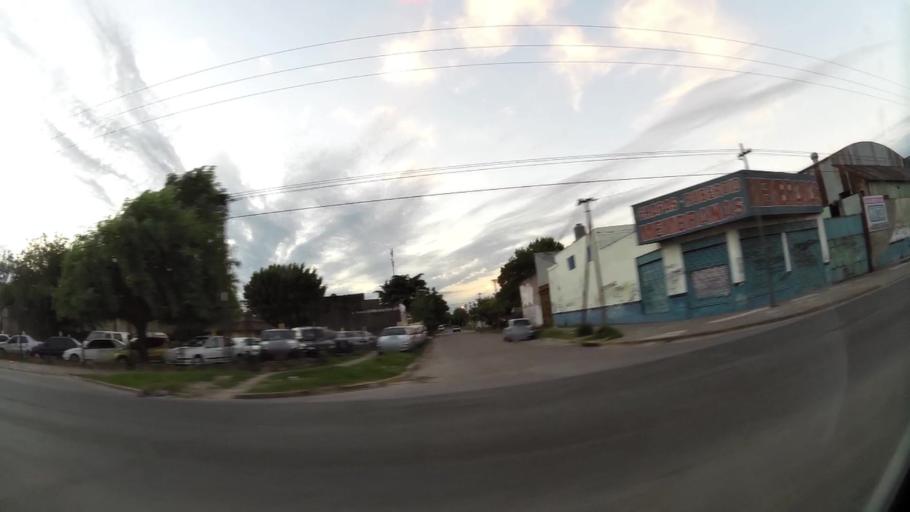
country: AR
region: Buenos Aires
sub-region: Partido de Merlo
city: Merlo
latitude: -34.6707
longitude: -58.7477
